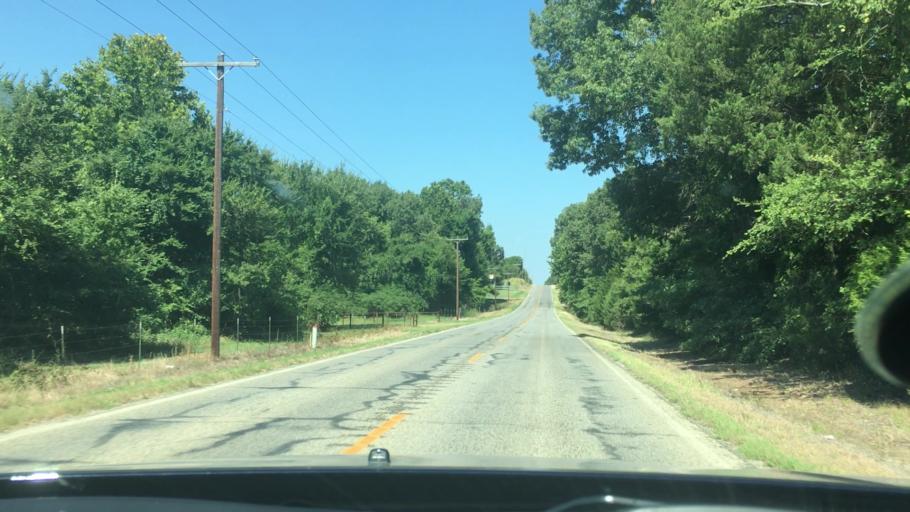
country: US
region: Oklahoma
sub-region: Johnston County
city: Tishomingo
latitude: 34.2378
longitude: -96.5912
